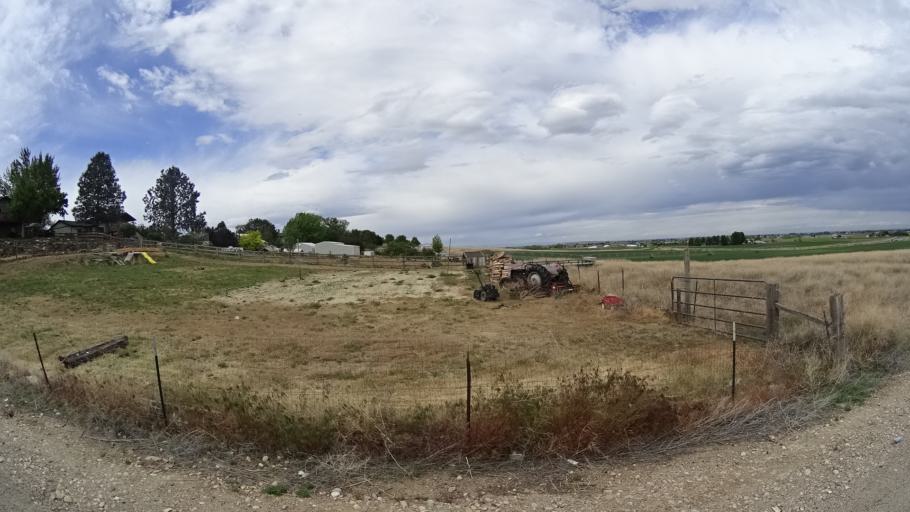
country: US
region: Idaho
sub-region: Ada County
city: Kuna
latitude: 43.4601
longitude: -116.4437
